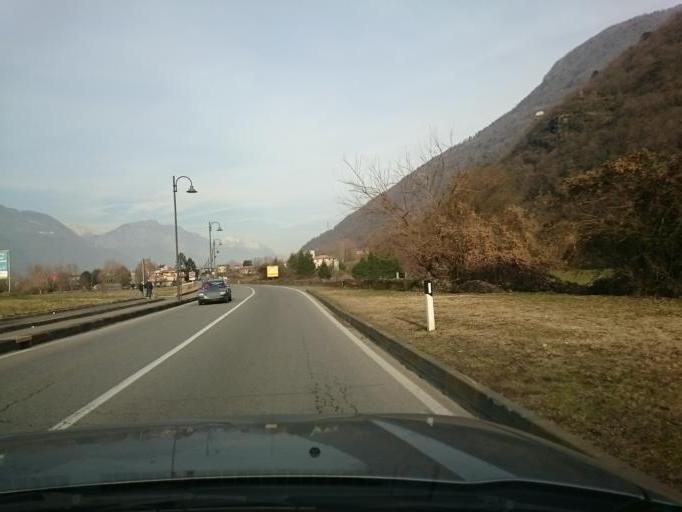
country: IT
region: Lombardy
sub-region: Provincia di Brescia
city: Pisogne
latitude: 45.8120
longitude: 10.1137
